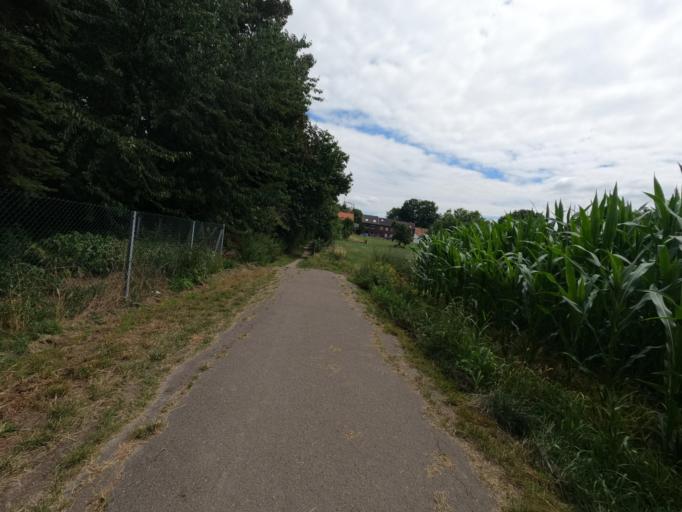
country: DE
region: North Rhine-Westphalia
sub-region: Regierungsbezirk Koln
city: Heinsberg
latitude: 51.0517
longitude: 6.1283
